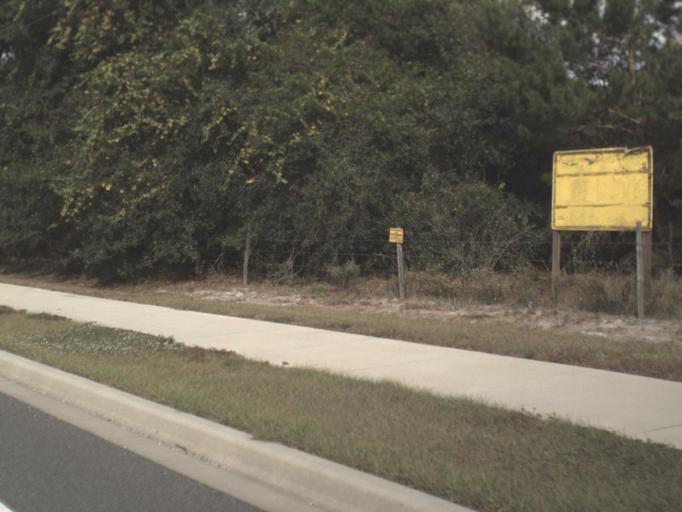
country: US
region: Florida
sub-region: Osceola County
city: Saint Cloud
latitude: 28.3334
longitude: -81.2282
